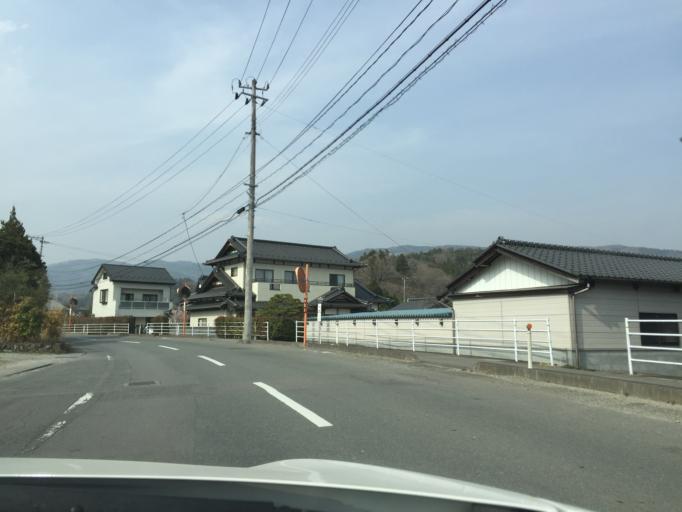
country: JP
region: Fukushima
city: Iwaki
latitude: 37.0150
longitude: 140.7369
